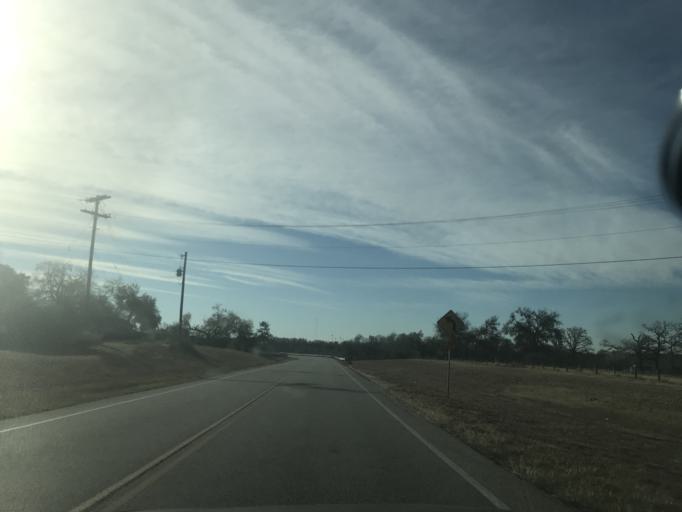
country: US
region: Texas
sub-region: Travis County
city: Manor
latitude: 30.2889
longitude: -97.5229
